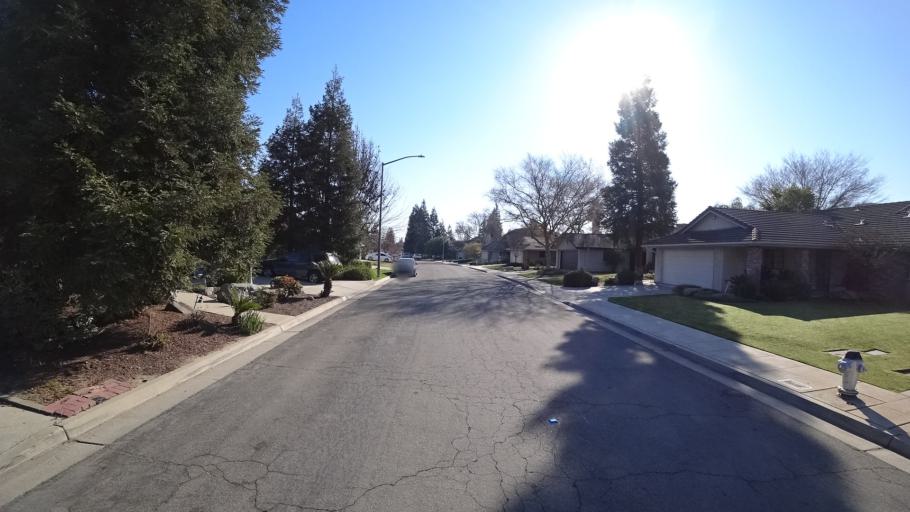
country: US
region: California
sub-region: Fresno County
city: Clovis
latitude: 36.8700
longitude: -119.7459
